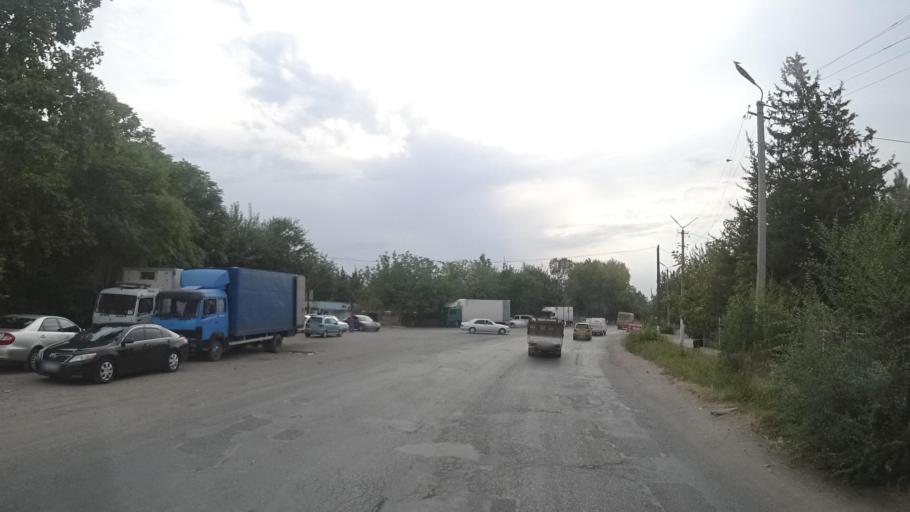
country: KG
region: Jalal-Abad
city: Massy
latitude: 41.0631
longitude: 72.6396
